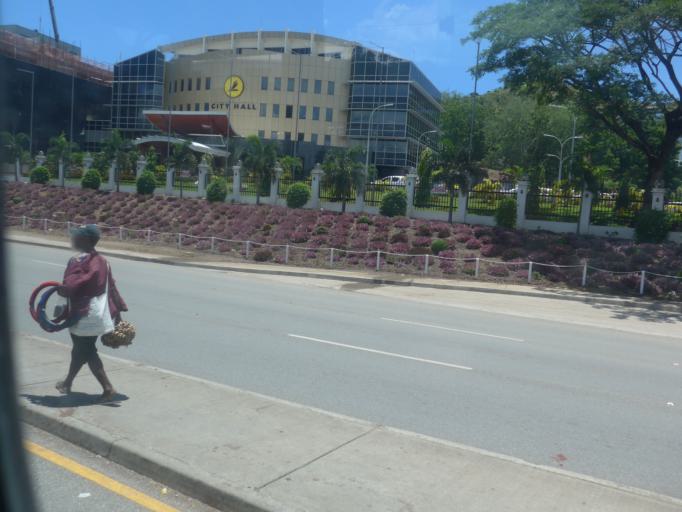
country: PG
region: National Capital
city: Port Moresby
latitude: -9.4394
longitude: 147.1805
